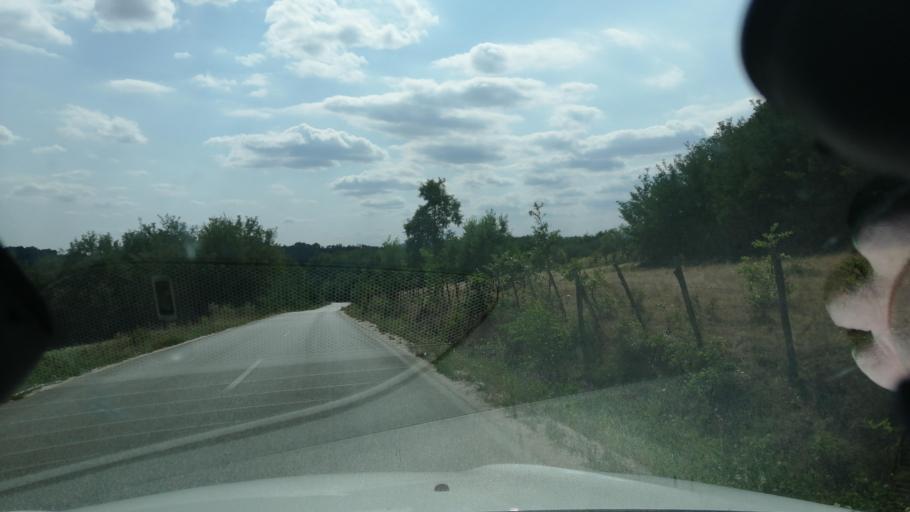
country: RS
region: Central Serbia
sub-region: Moravicki Okrug
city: Cacak
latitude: 43.8050
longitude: 20.2679
